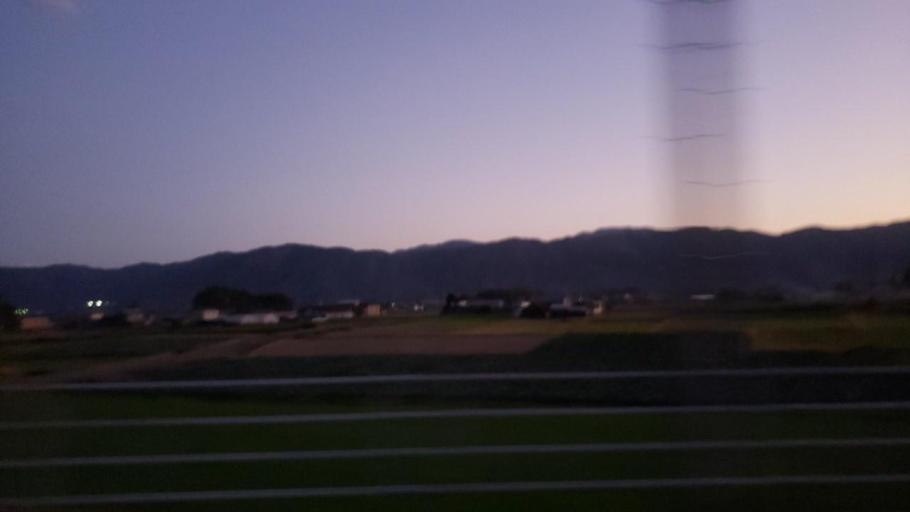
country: JP
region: Tokushima
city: Kamojimacho-jogejima
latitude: 34.0857
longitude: 134.2883
